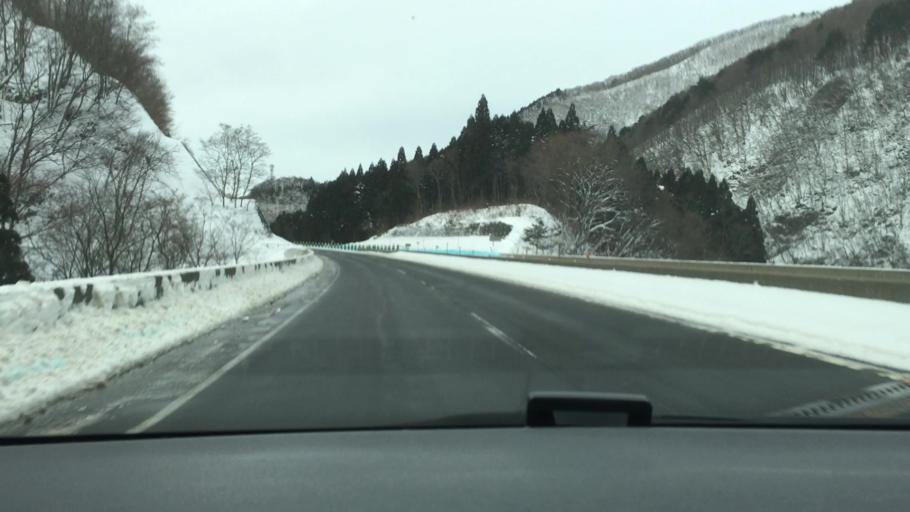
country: JP
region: Akita
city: Hanawa
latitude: 40.1197
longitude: 140.8530
